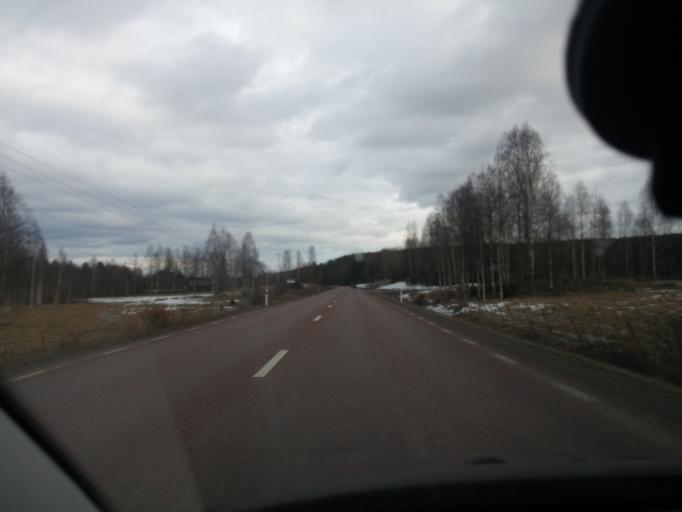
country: SE
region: Gaevleborg
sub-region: Ljusdals Kommun
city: Ljusdal
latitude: 61.8118
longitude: 16.0901
